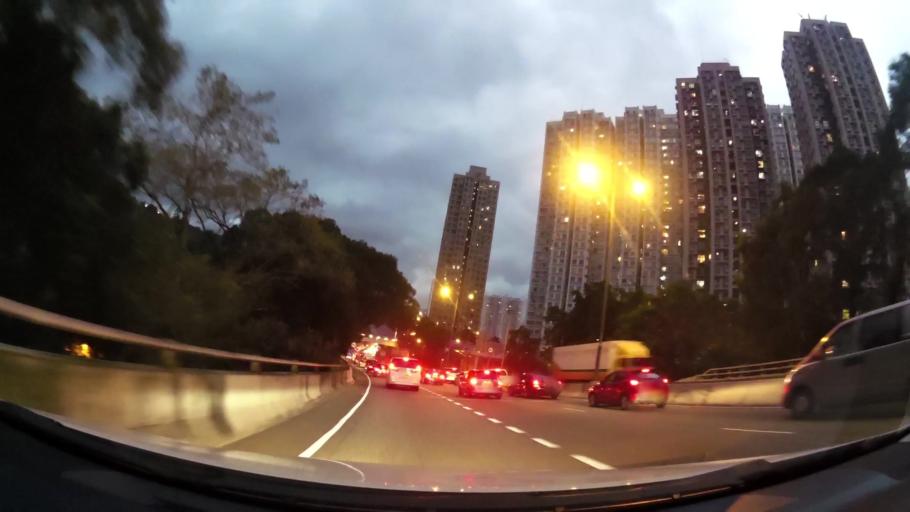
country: HK
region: Sha Tin
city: Sha Tin
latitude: 22.3791
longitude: 114.1852
